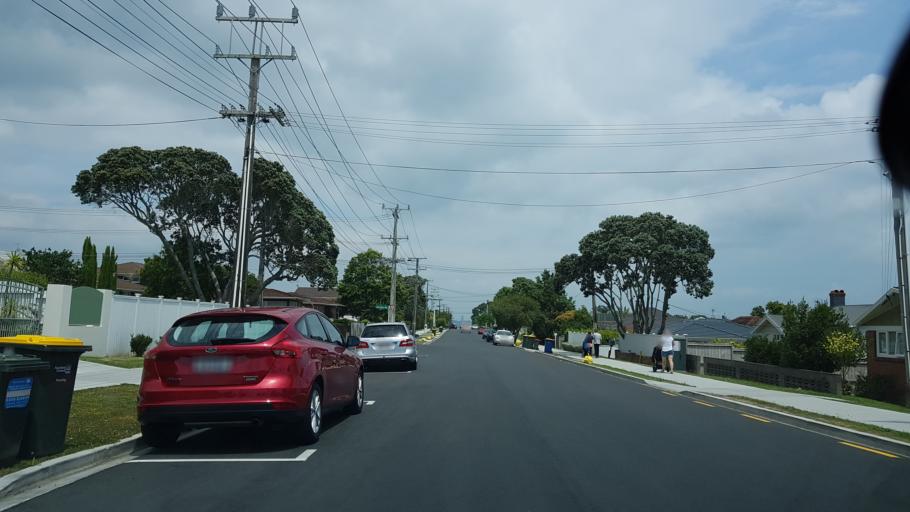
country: NZ
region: Auckland
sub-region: Auckland
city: North Shore
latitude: -36.7990
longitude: 174.7777
